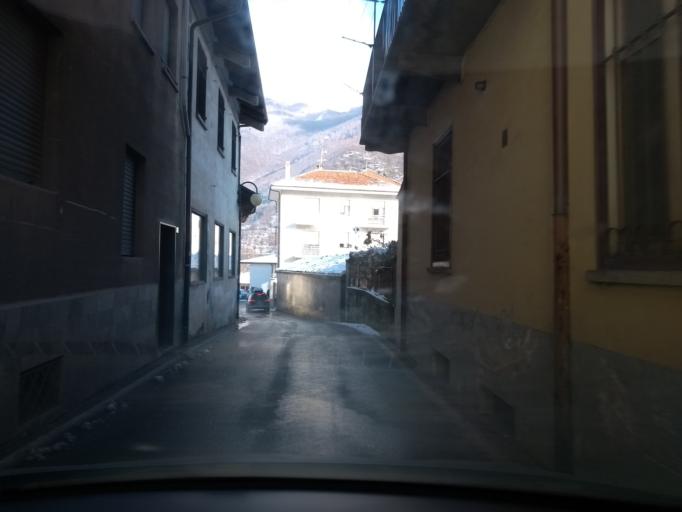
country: IT
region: Piedmont
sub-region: Provincia di Torino
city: Ceres
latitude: 45.3138
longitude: 7.3889
